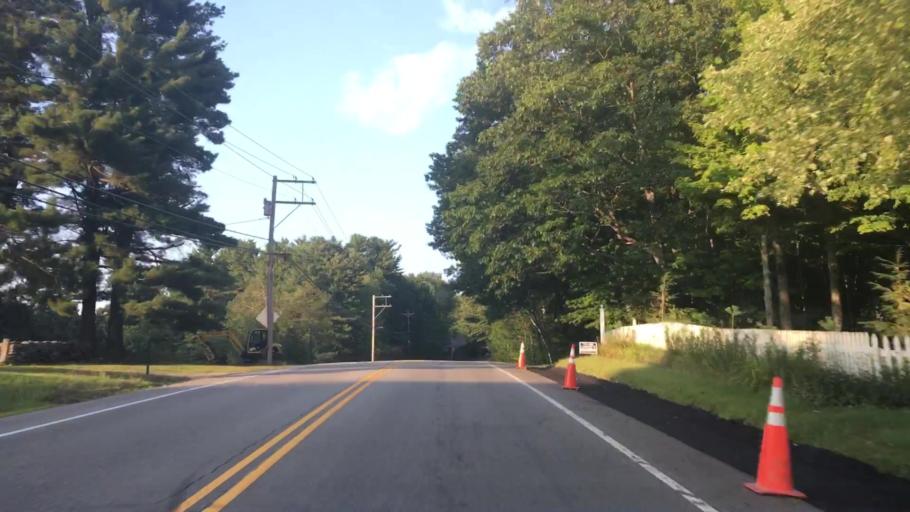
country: US
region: New Hampshire
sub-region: Belknap County
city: Gilmanton
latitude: 43.4259
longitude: -71.4115
